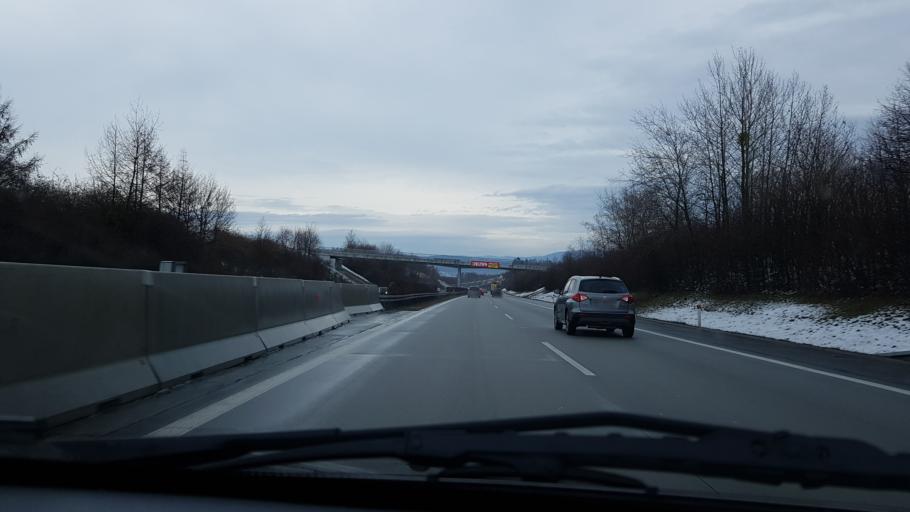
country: CZ
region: Olomoucky
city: Dolni Ujezd
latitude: 49.5561
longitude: 17.5233
